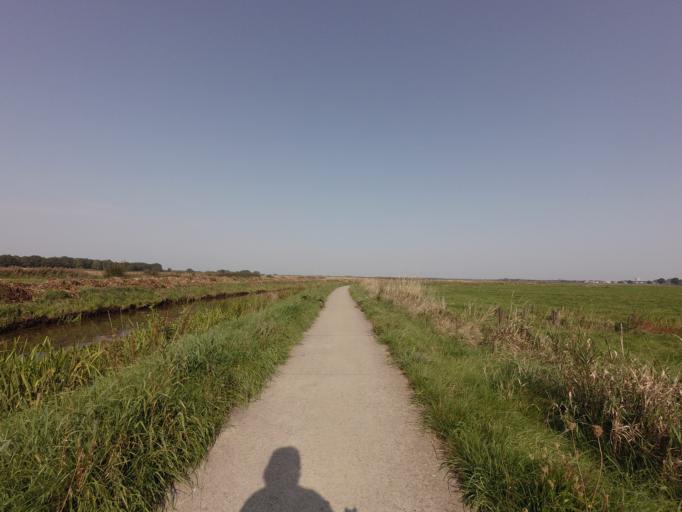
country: NL
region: Groningen
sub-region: Gemeente Groningen
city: Groningen
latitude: 53.1565
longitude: 6.5377
